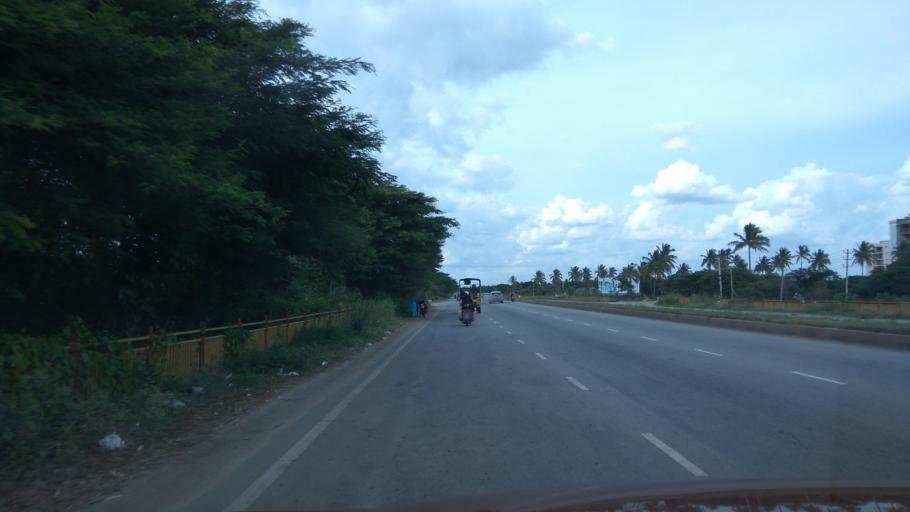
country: IN
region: Karnataka
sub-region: Bangalore Rural
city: Devanhalli
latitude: 13.2323
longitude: 77.6928
